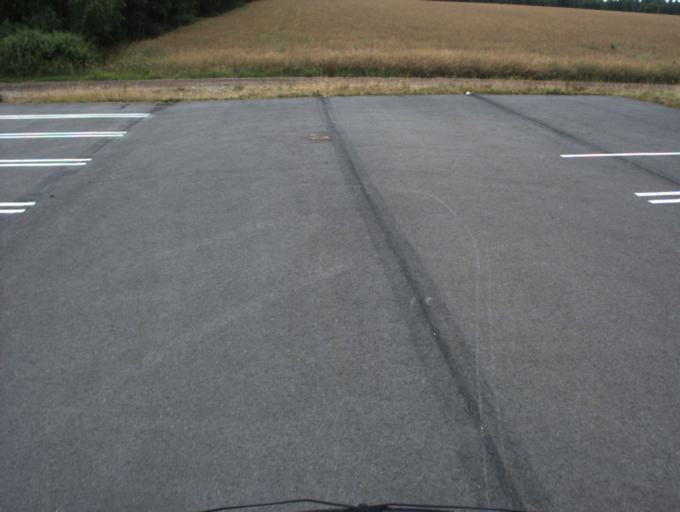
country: SE
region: Skane
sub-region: Helsingborg
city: Odakra
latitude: 56.0810
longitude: 12.7418
